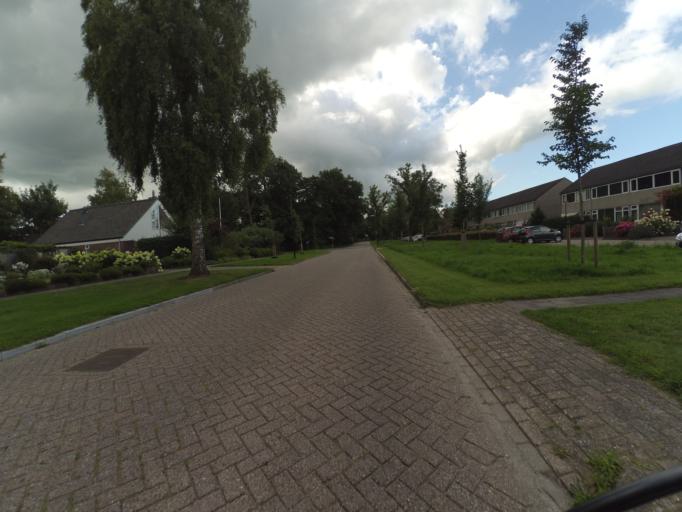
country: NL
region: Friesland
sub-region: Gemeente Tytsjerksteradiel
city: Hurdegaryp
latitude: 53.2113
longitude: 5.9411
